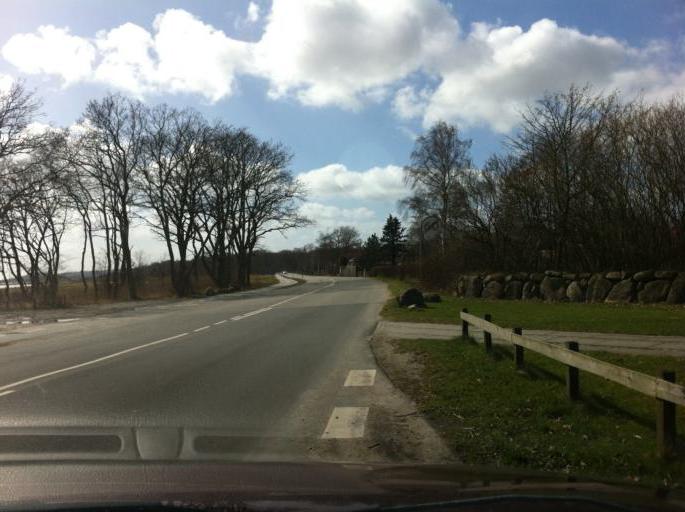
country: DK
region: Central Jutland
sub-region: Syddjurs Kommune
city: Ebeltoft
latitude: 56.2290
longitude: 10.6053
